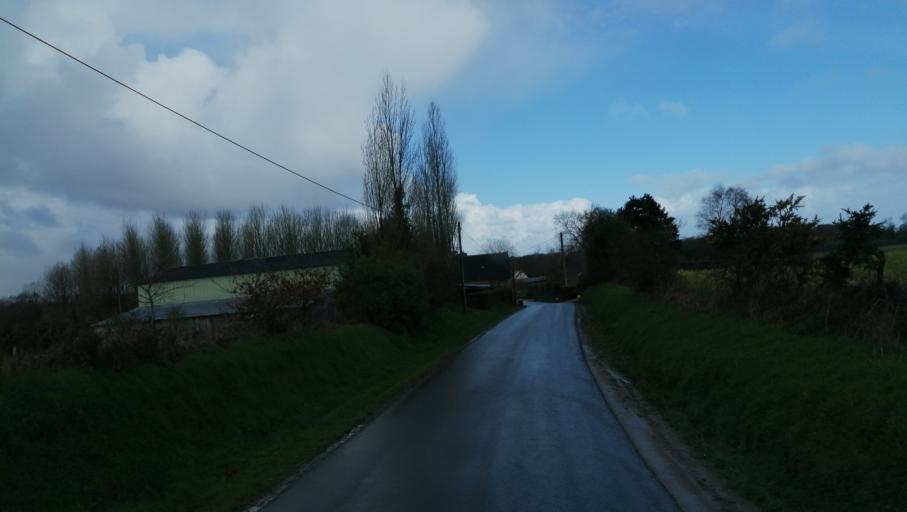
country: FR
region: Brittany
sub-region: Departement des Cotes-d'Armor
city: Lanrodec
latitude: 48.4941
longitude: -3.0110
